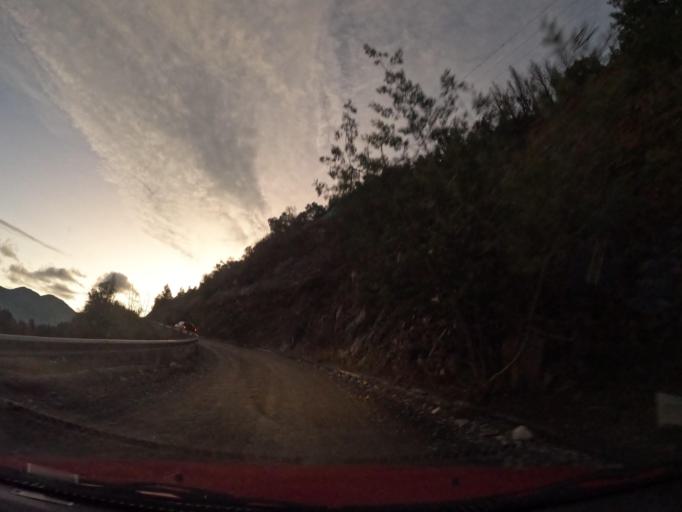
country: CL
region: Maule
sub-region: Provincia de Linares
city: Colbun
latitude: -35.8574
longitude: -71.2217
